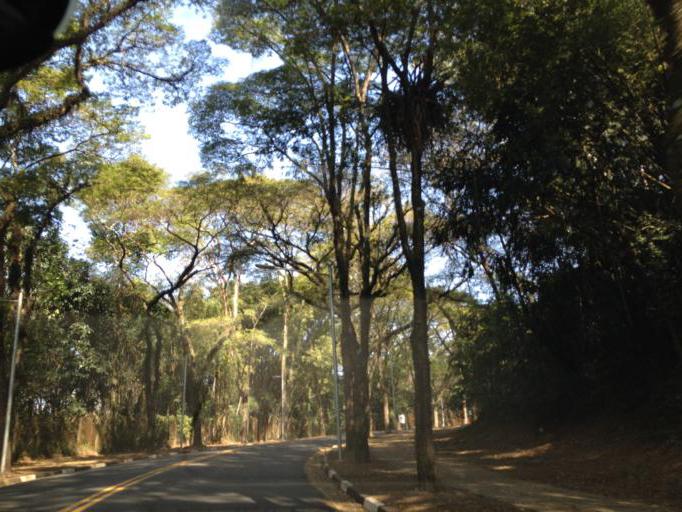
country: BR
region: Sao Paulo
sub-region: Osasco
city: Osasco
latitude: -23.5644
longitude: -46.7289
